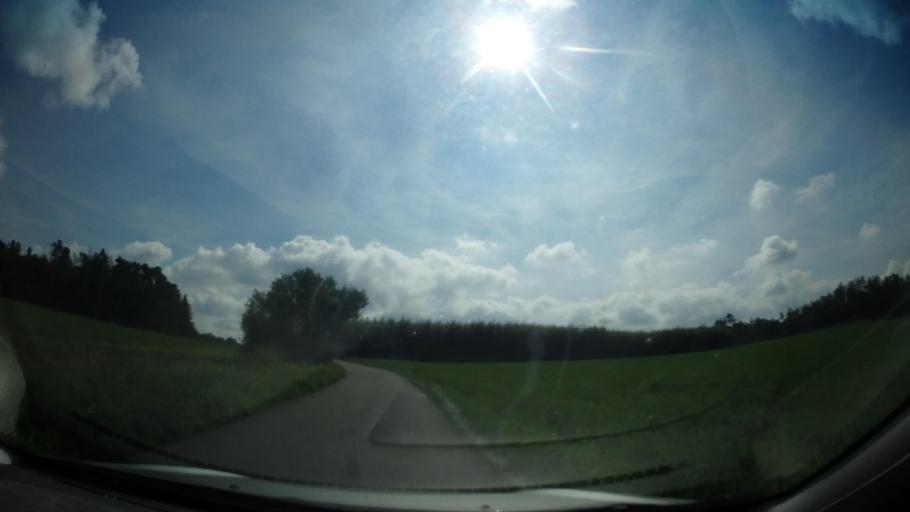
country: CZ
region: Central Bohemia
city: Krasna Hora nad Vltavou
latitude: 49.6887
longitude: 14.3209
